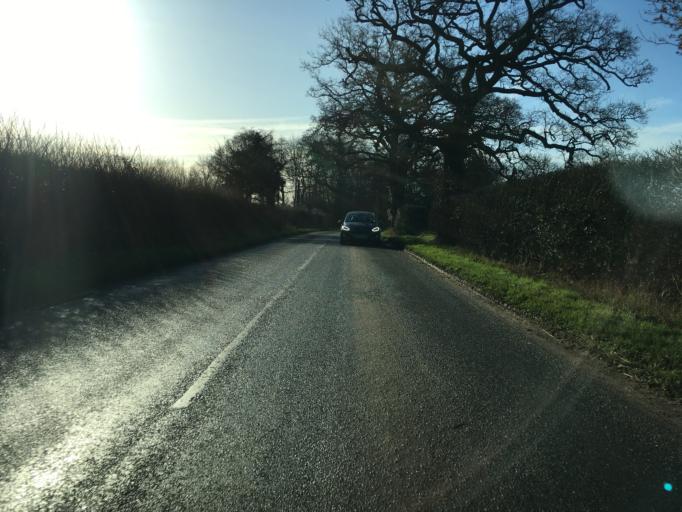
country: GB
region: England
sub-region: Warwickshire
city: Wellesbourne Mountford
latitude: 52.2124
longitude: -1.6100
